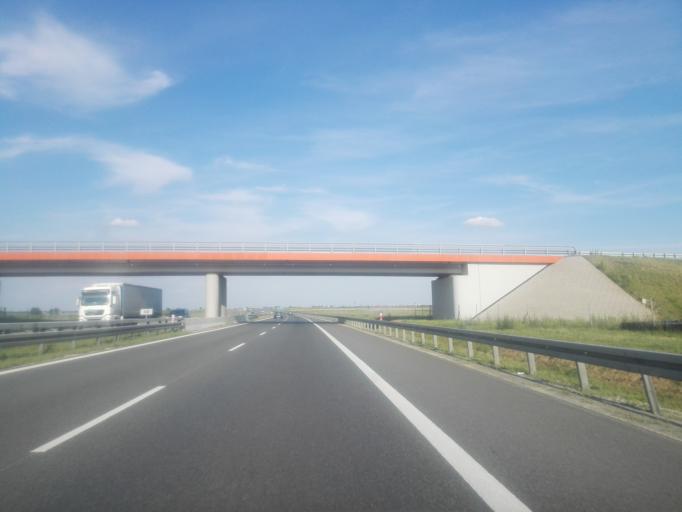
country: PL
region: Lower Silesian Voivodeship
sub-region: Powiat olesnicki
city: Dobroszyce
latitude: 51.2217
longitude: 17.3181
